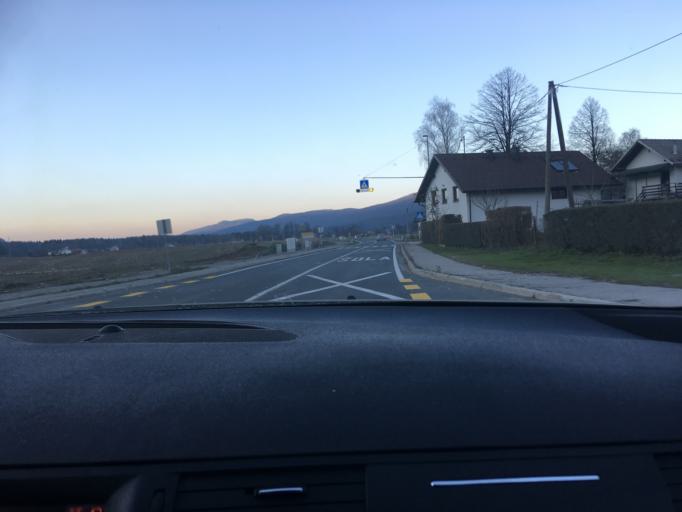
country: SI
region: Kocevje
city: Kocevje
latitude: 45.6682
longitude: 14.8374
